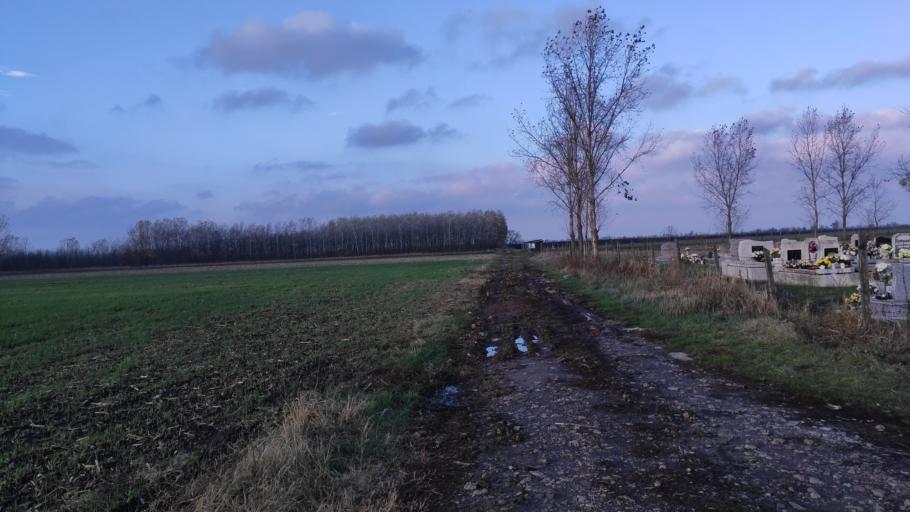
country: HU
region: Bekes
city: Mezobereny
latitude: 46.7620
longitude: 21.0518
